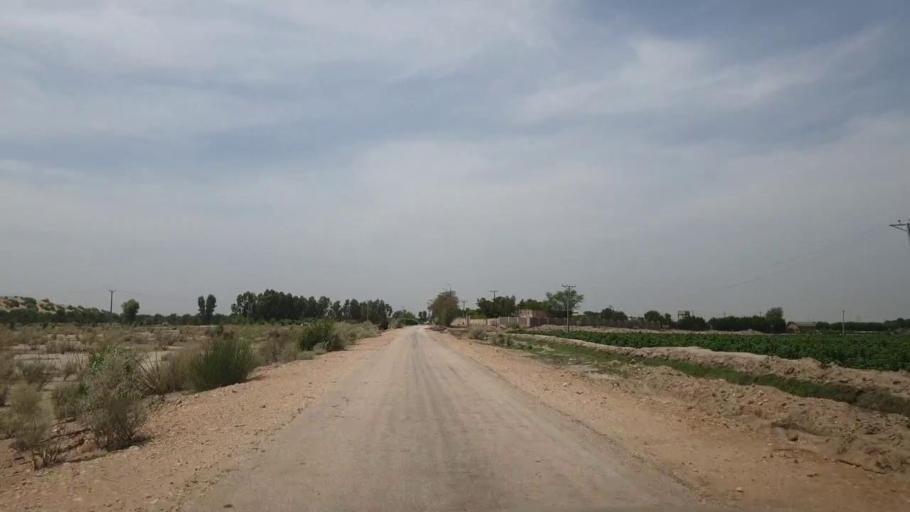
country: PK
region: Sindh
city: Kot Diji
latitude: 27.0937
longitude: 69.0769
